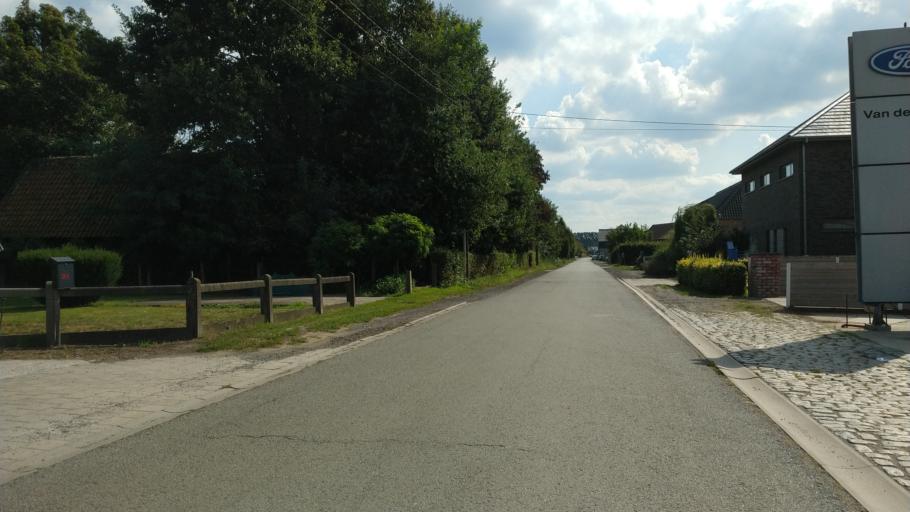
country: BE
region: Flanders
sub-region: Provincie Oost-Vlaanderen
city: Kaprijke
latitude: 51.1944
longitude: 3.6800
